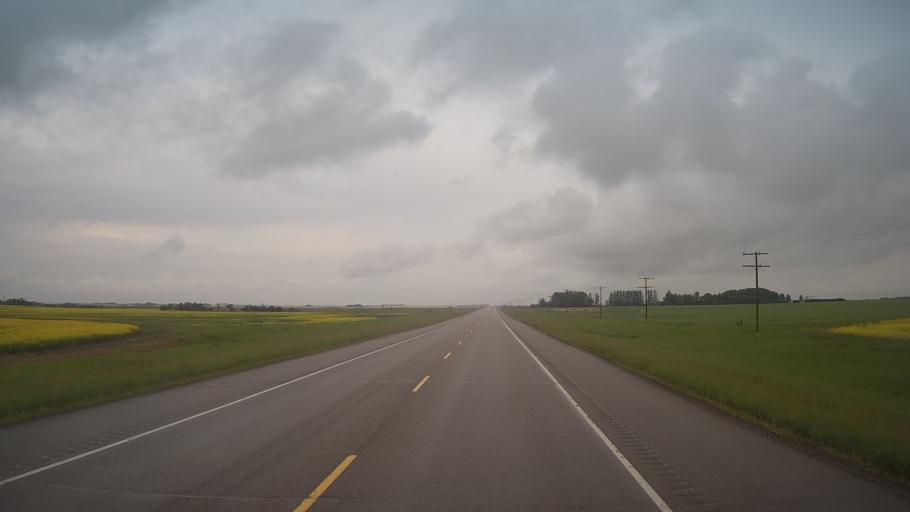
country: CA
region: Saskatchewan
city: Unity
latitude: 52.4349
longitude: -108.9645
